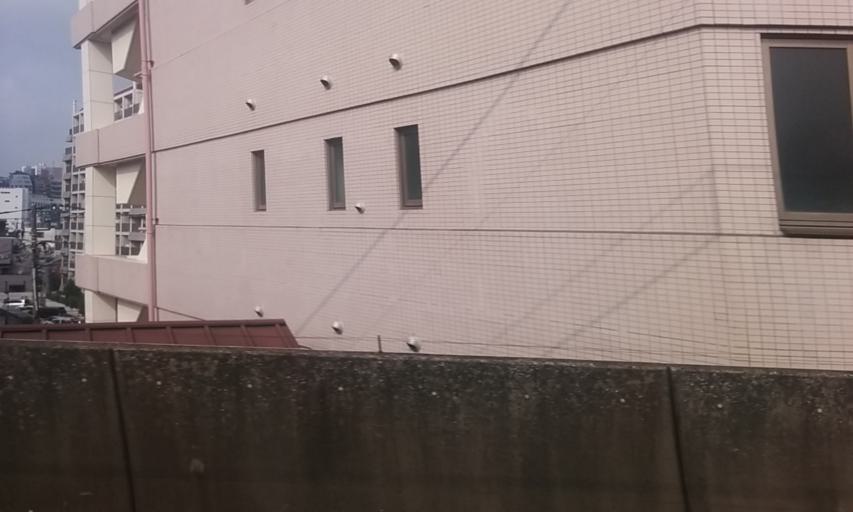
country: JP
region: Kanagawa
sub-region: Kawasaki-shi
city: Kawasaki
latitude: 35.6106
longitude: 139.7427
